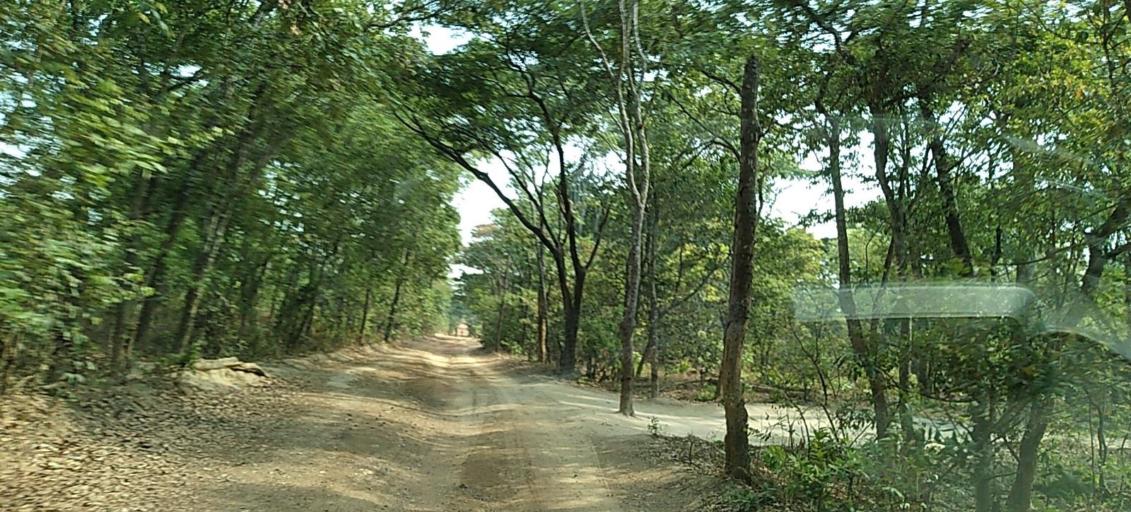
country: ZM
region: Copperbelt
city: Kalulushi
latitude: -12.9201
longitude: 27.8224
